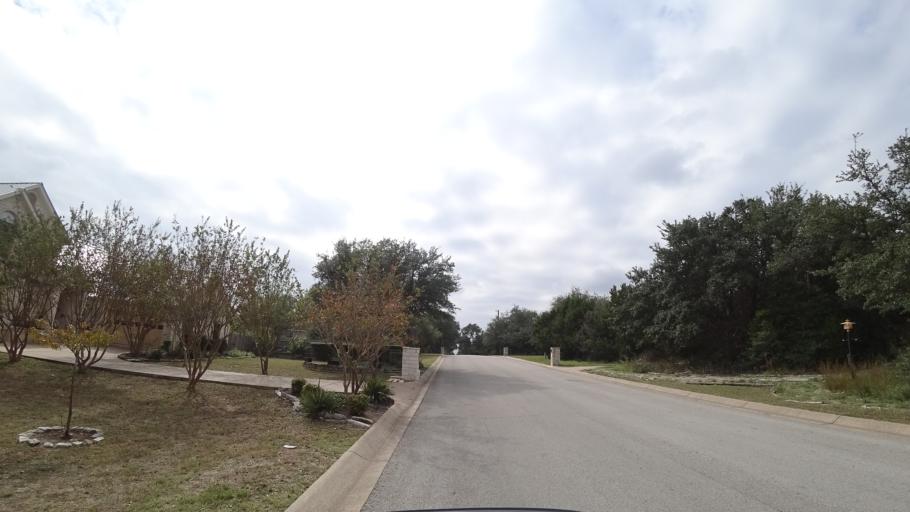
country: US
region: Texas
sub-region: Travis County
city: Shady Hollow
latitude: 30.2206
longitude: -97.8948
